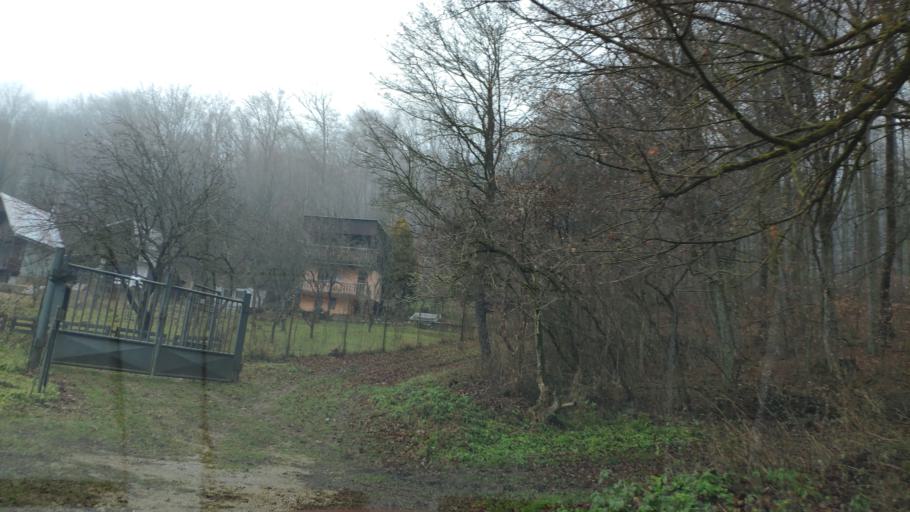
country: SK
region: Banskobystricky
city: Revuca
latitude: 48.6522
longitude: 20.2629
